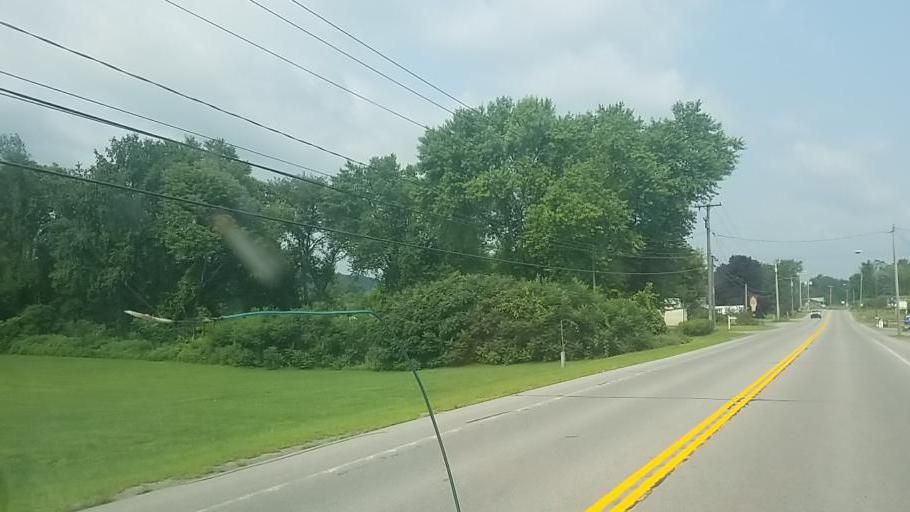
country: US
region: New York
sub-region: Montgomery County
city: Canajoharie
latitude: 42.9183
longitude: -74.5944
